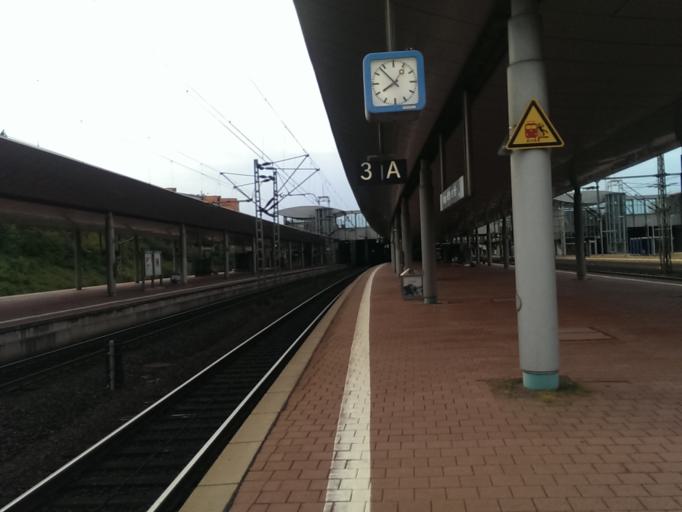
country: DE
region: Hesse
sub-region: Regierungsbezirk Kassel
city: Kassel
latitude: 51.3095
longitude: 9.4486
